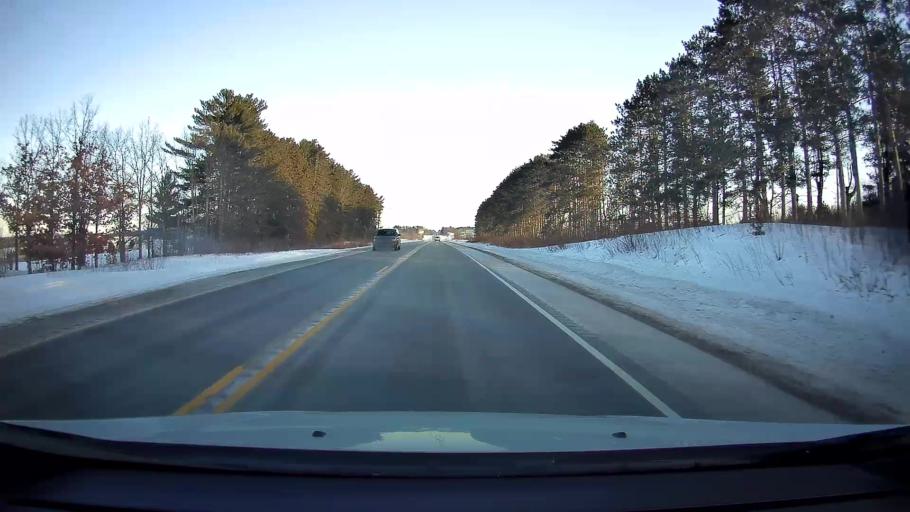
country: US
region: Wisconsin
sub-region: Washburn County
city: Shell Lake
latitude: 45.7617
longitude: -91.9134
